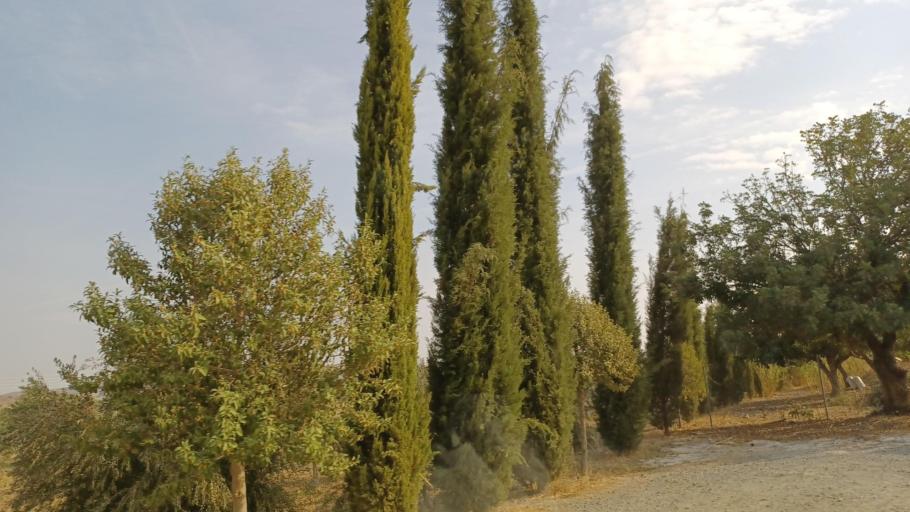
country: CY
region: Larnaka
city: Troulloi
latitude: 35.0269
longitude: 33.6058
